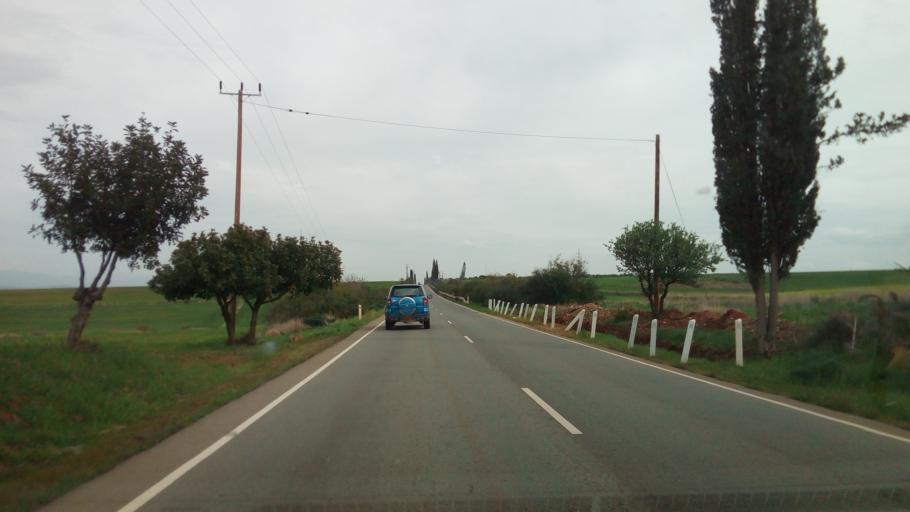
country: CY
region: Lefkosia
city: Astromeritis
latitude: 35.1144
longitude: 32.9958
